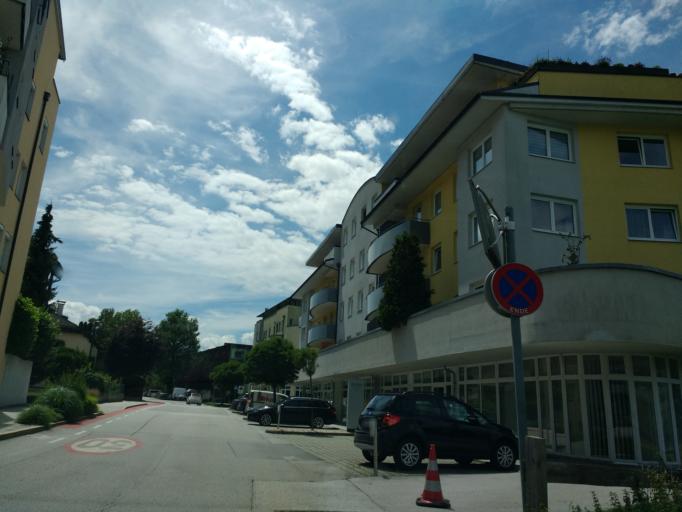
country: AT
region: Tyrol
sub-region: Politischer Bezirk Kufstein
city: Kufstein
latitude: 47.5850
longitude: 12.1747
